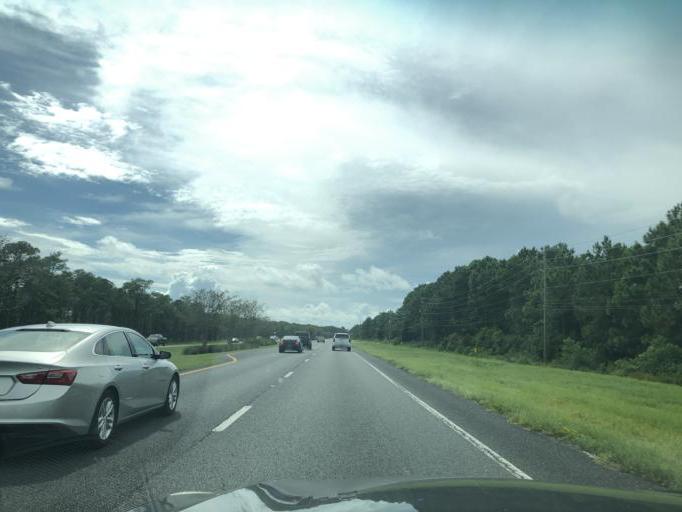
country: US
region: Florida
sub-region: Walton County
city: Miramar Beach
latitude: 30.3759
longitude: -86.2941
